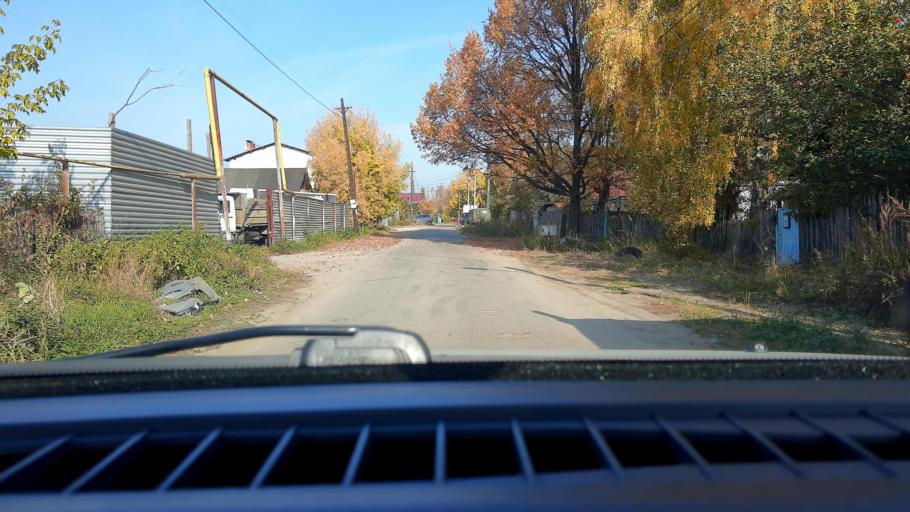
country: RU
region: Nizjnij Novgorod
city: Gorbatovka
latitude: 56.3299
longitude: 43.8298
